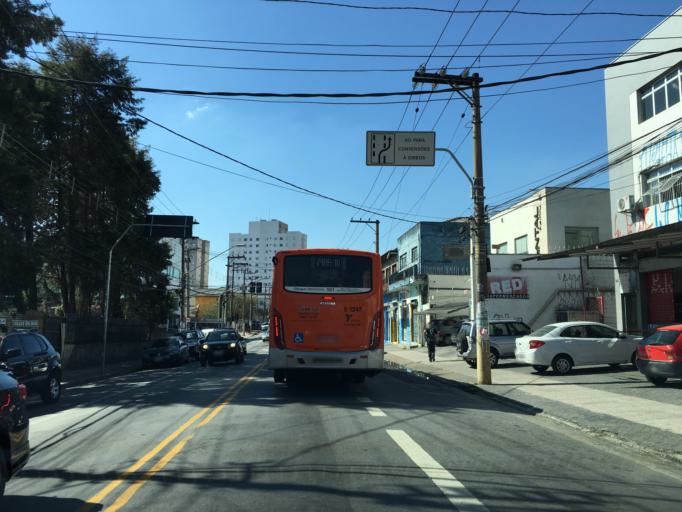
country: BR
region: Sao Paulo
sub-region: Osasco
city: Osasco
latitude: -23.5644
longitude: -46.7497
